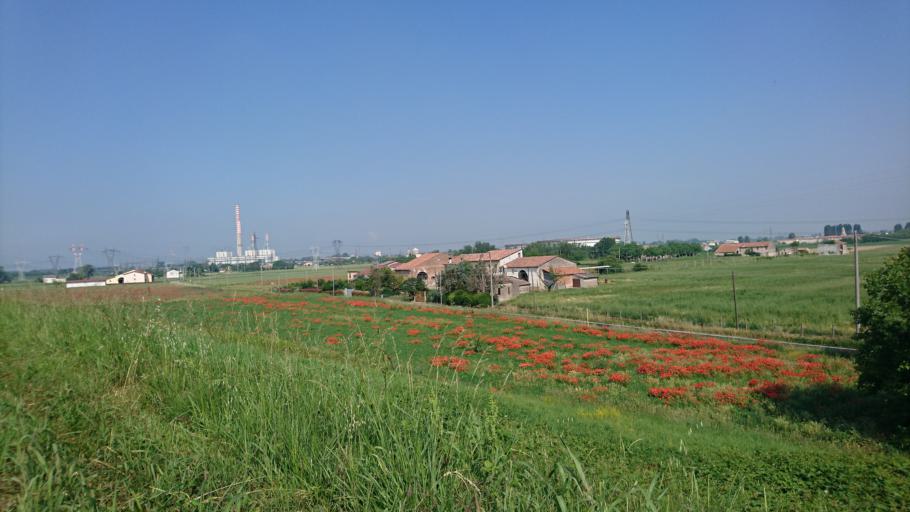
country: IT
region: Lombardy
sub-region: Provincia di Mantova
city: Ostiglia
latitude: 45.0572
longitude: 11.1608
